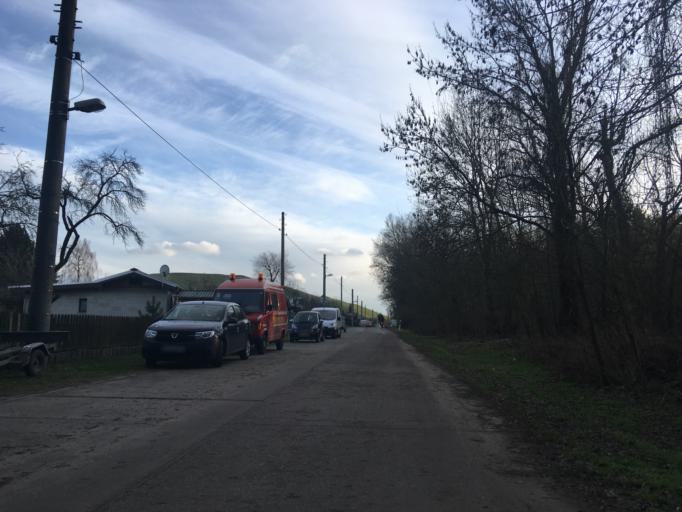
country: DE
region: Berlin
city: Blankenfelde
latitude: 52.6434
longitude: 13.3986
